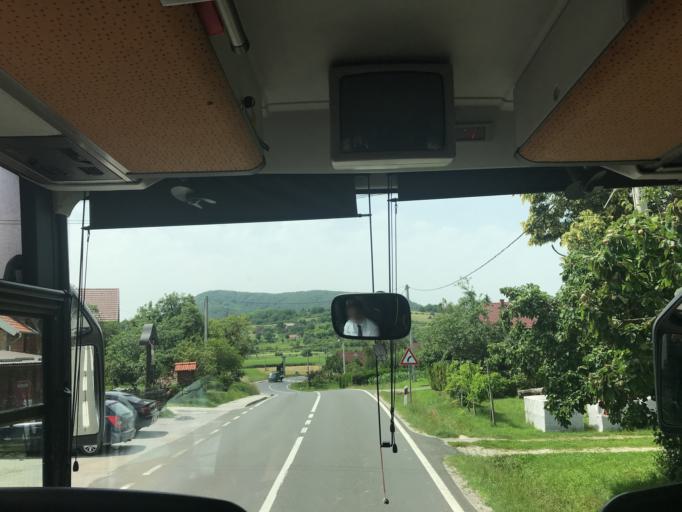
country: HR
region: Varazdinska
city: Lepoglava
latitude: 46.2138
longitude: 16.0113
